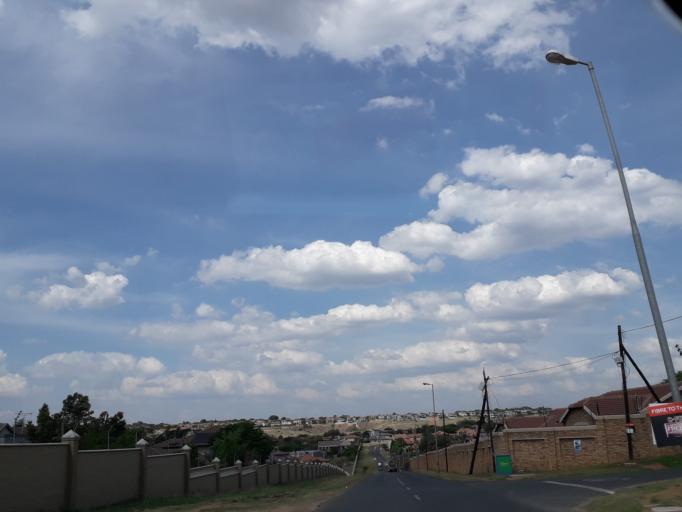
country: ZA
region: Gauteng
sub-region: City of Johannesburg Metropolitan Municipality
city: Roodepoort
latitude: -26.0907
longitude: 27.9087
